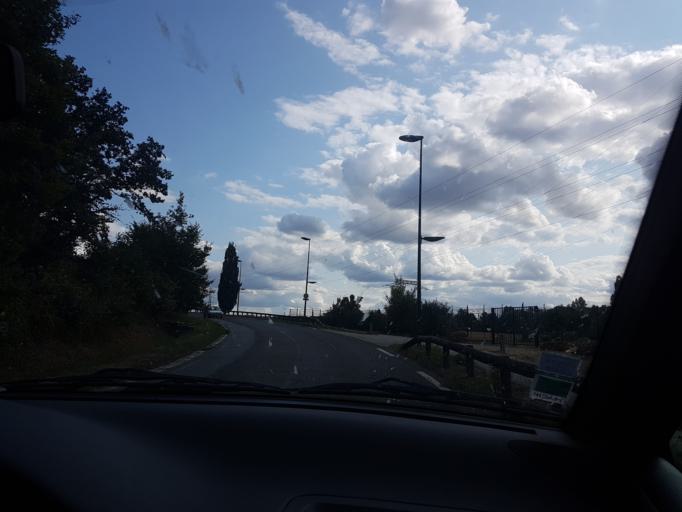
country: FR
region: Ile-de-France
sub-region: Departement des Yvelines
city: Plaisir
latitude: 48.8092
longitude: 1.9446
